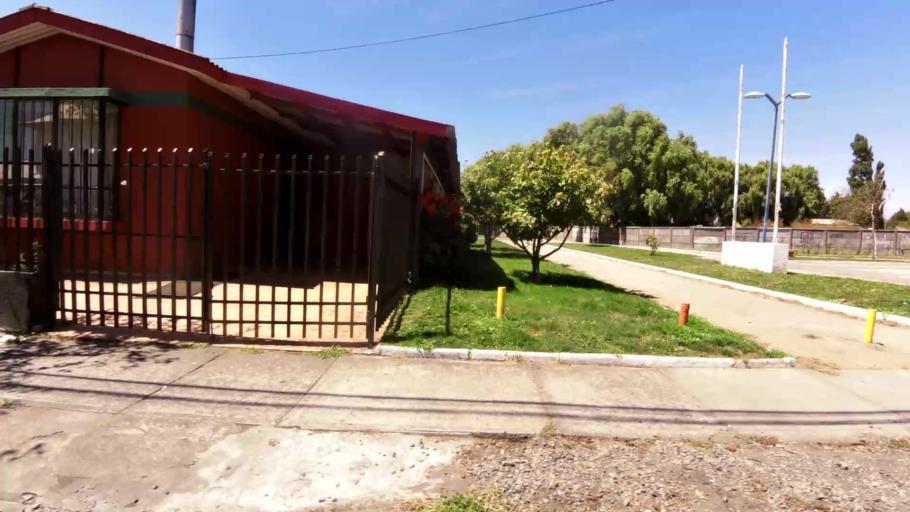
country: CL
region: Biobio
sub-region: Provincia de Concepcion
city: Talcahuano
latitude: -36.7564
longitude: -73.0829
